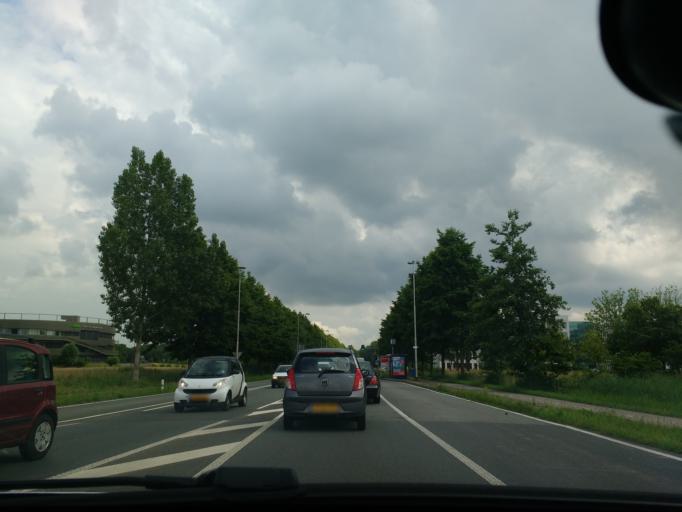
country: NL
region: Gelderland
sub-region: Gemeente Ede
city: Bennekom
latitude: 51.9871
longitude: 5.6698
